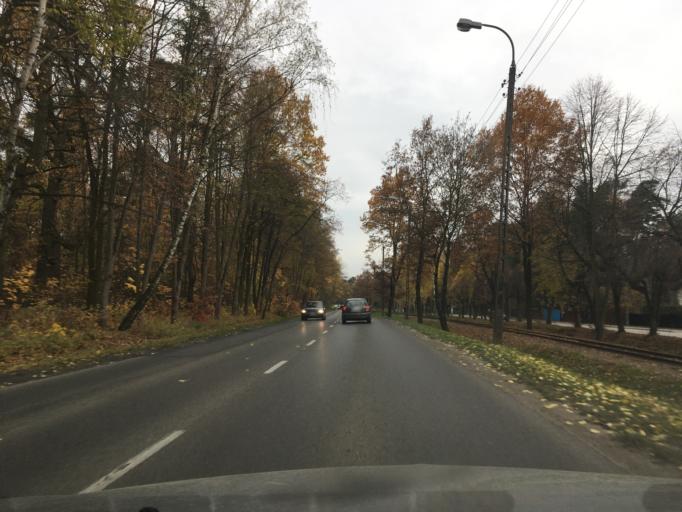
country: PL
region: Masovian Voivodeship
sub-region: Powiat piaseczynski
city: Piaseczno
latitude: 52.0624
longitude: 21.0146
